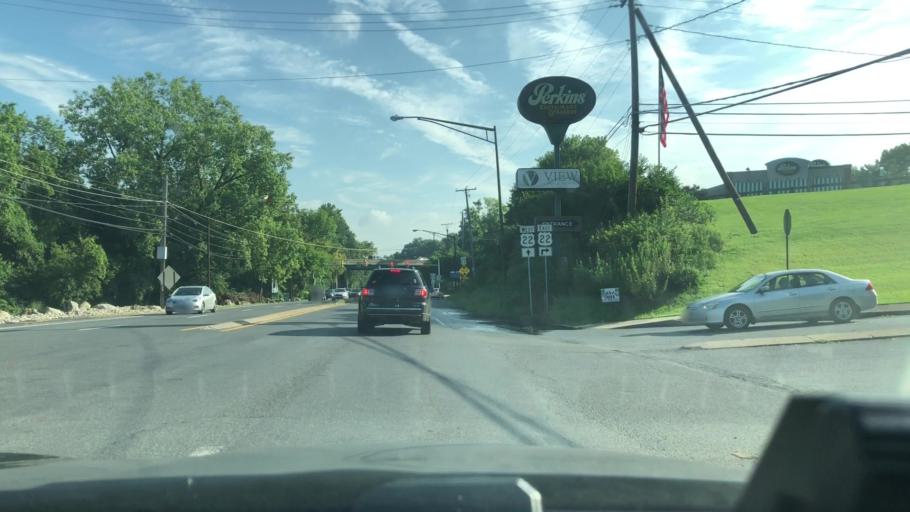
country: US
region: Pennsylvania
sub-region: Northampton County
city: Middletown
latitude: 40.6768
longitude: -75.3435
